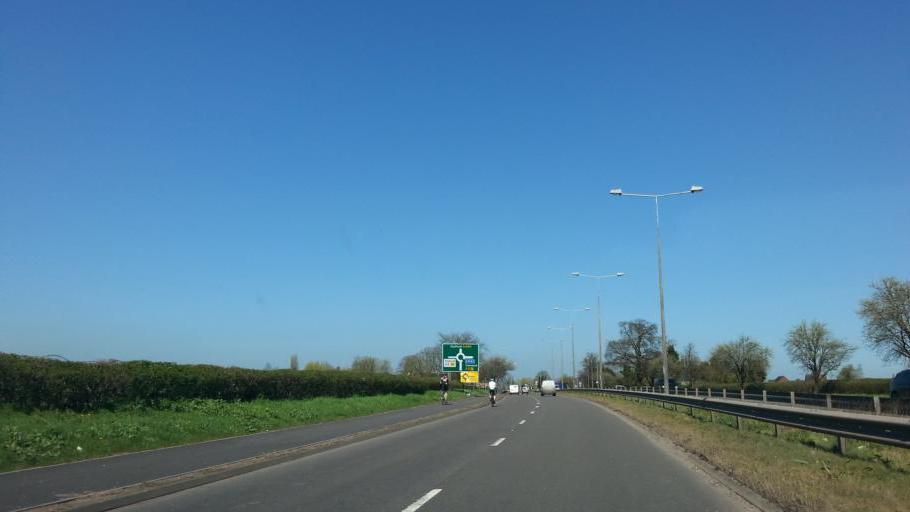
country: GB
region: England
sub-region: Staffordshire
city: Penkridge
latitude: 52.6905
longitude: -2.1318
